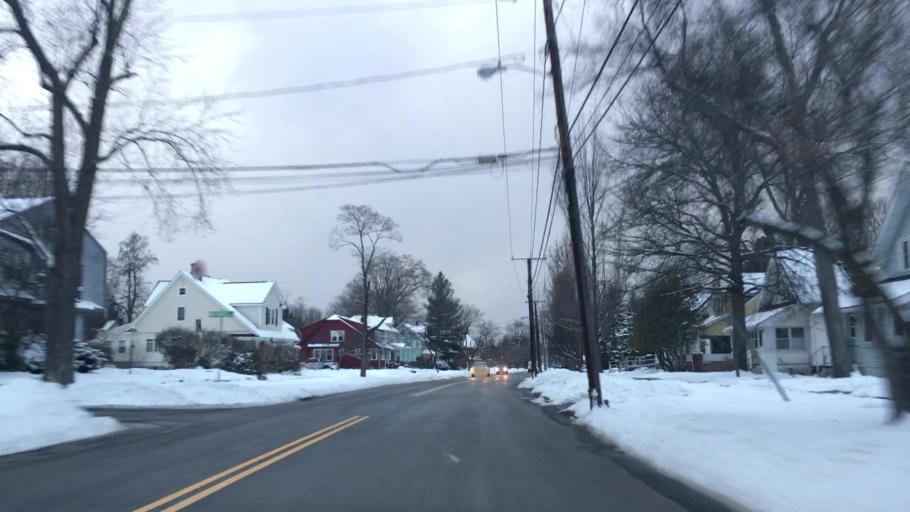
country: US
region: Massachusetts
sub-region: Hampden County
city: Longmeadow
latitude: 42.0573
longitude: -72.5749
